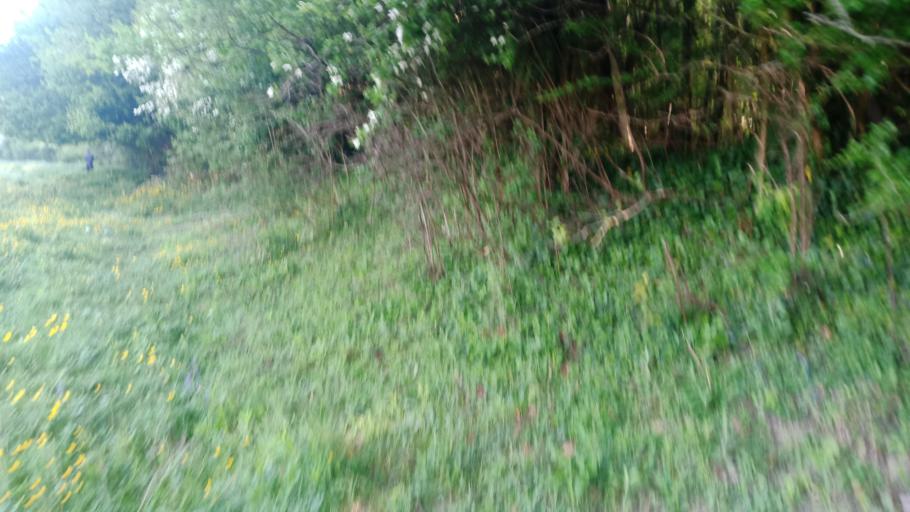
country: FR
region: Rhone-Alpes
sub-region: Departement de l'Isere
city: Serpaize
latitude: 45.5468
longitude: 4.9396
